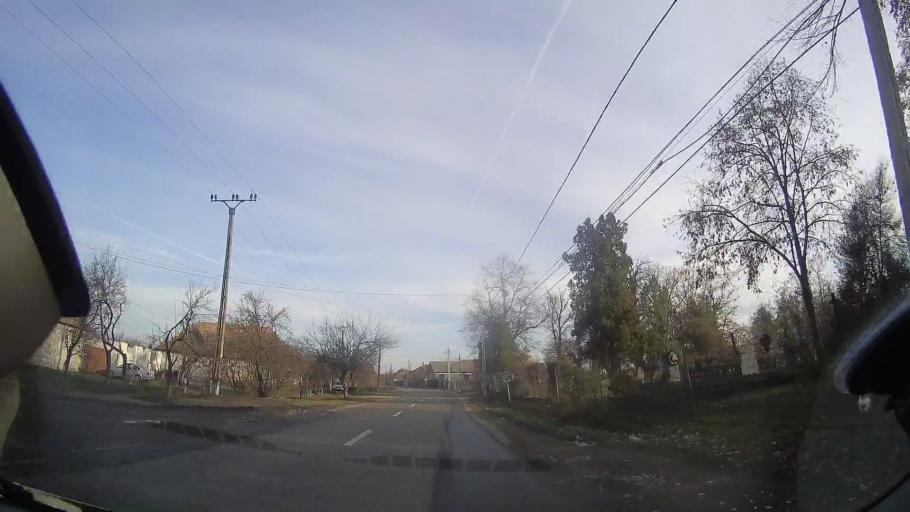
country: RO
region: Bihor
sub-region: Comuna Tileagd
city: Tileagd
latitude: 47.0690
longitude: 22.2017
